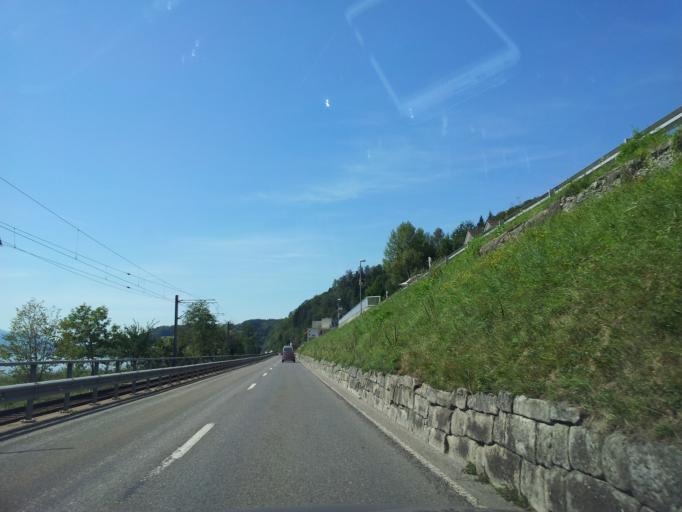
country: CH
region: Saint Gallen
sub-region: Wahlkreis See-Gaster
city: Schmerikon
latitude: 47.2259
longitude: 8.9335
